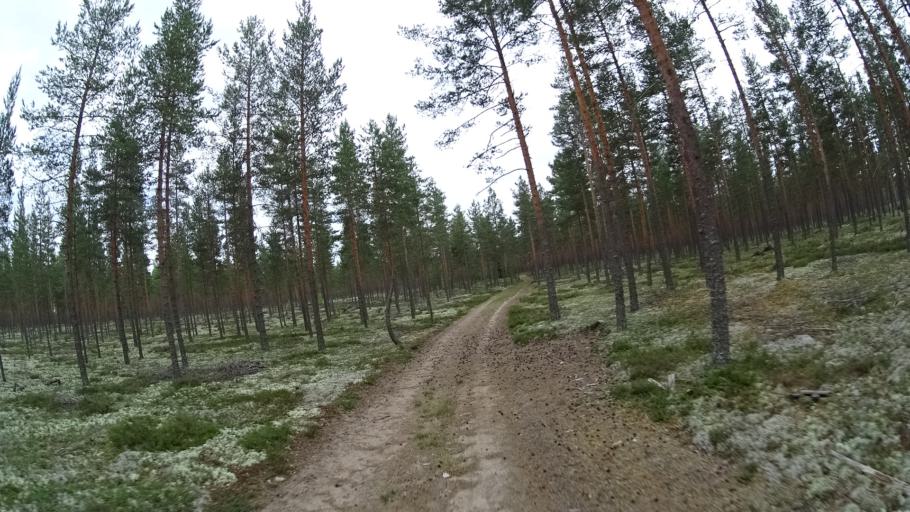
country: FI
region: Satakunta
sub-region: Pohjois-Satakunta
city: Jaemijaervi
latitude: 61.7706
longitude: 22.8019
